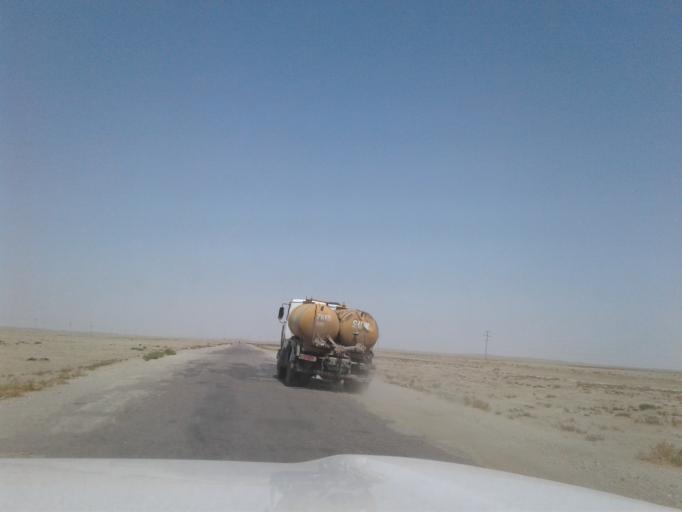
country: TM
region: Balkan
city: Gumdag
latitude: 38.3494
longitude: 54.3689
